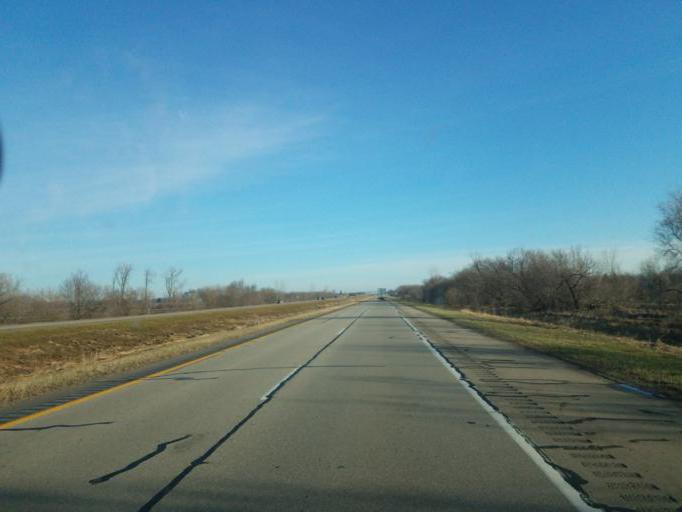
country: US
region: Michigan
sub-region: Clinton County
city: Saint Johns
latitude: 42.9692
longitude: -84.5185
